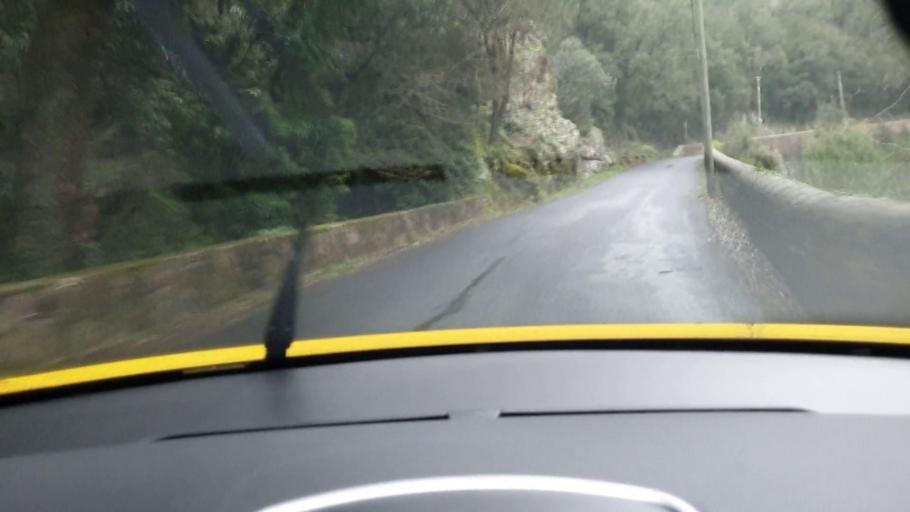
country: FR
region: Languedoc-Roussillon
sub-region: Departement du Gard
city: Sumene
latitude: 43.9929
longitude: 3.7116
